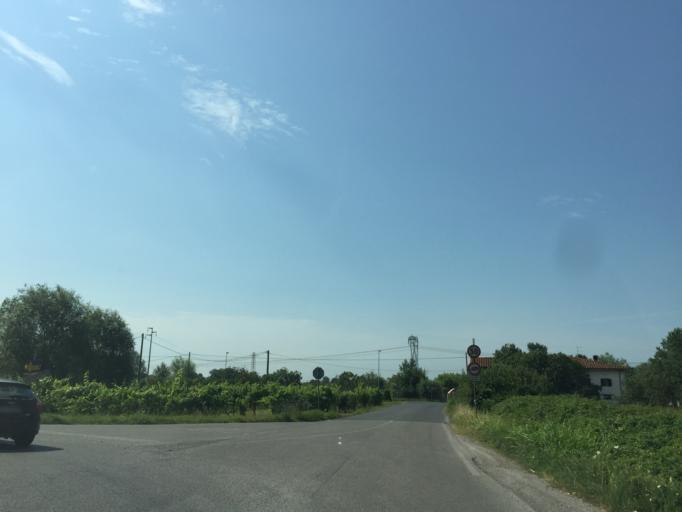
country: IT
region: Tuscany
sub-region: Provincia di Pistoia
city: Margine Coperta-Traversagna
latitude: 43.8631
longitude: 10.7537
